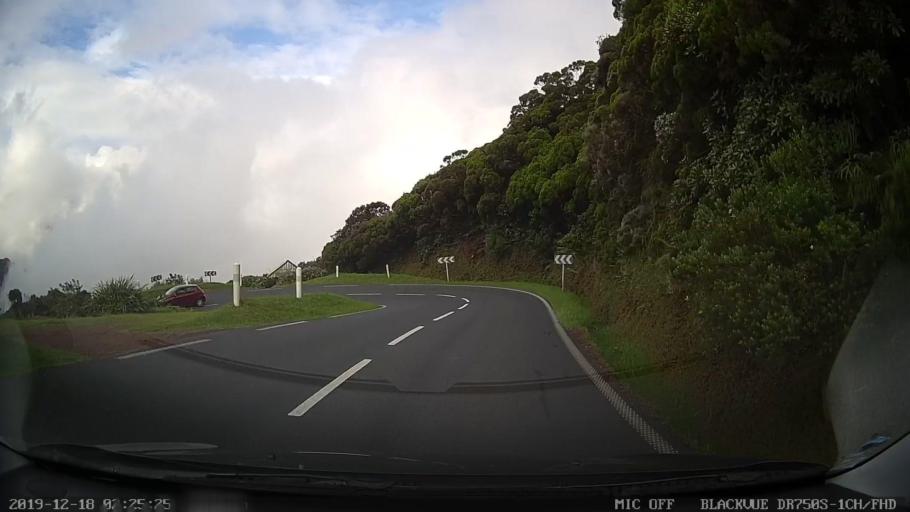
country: RE
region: Reunion
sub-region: Reunion
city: Cilaos
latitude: -21.1623
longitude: 55.6003
